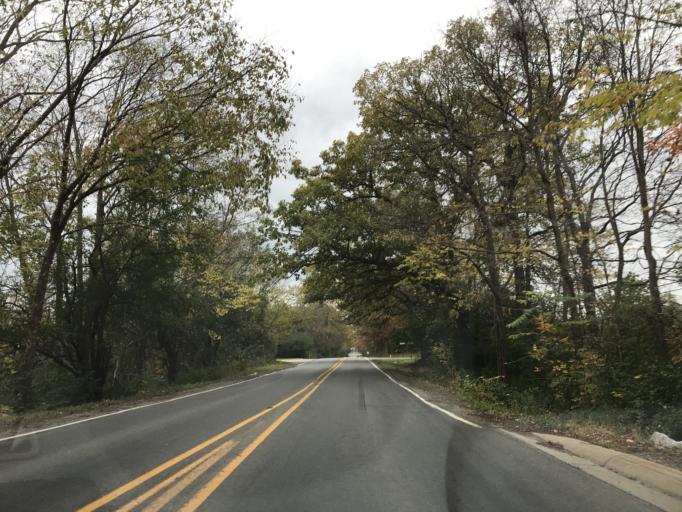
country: US
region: Michigan
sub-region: Washtenaw County
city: Ann Arbor
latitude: 42.2833
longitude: -83.6715
